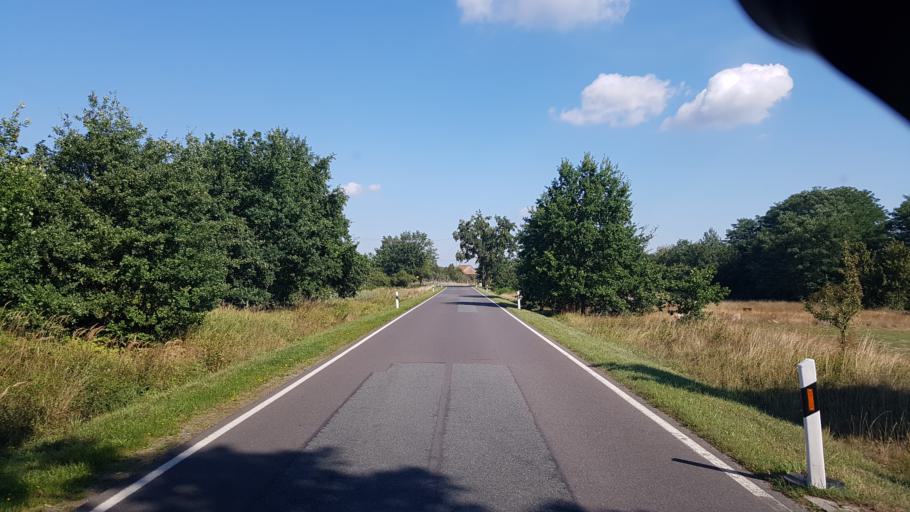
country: DE
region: Brandenburg
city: Altdobern
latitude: 51.7075
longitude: 14.0879
